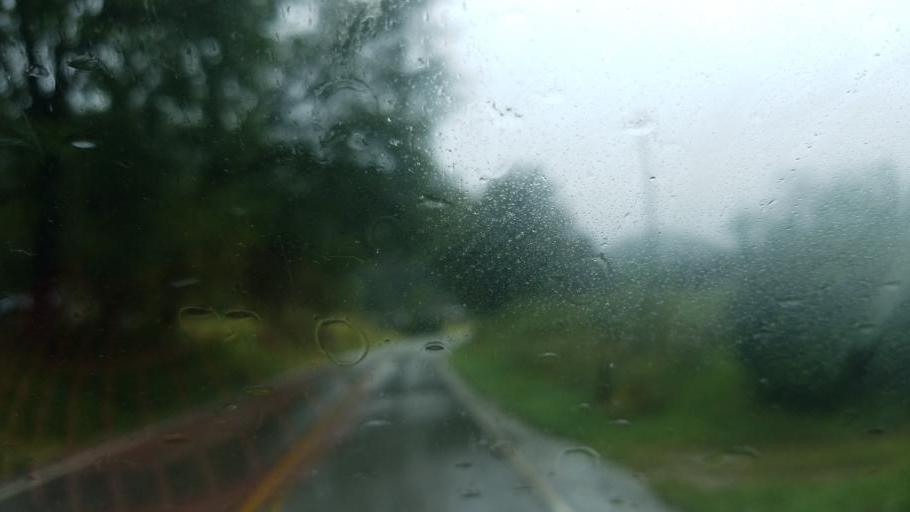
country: US
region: Kentucky
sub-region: Greenup County
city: South Shore
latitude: 38.6884
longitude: -82.9324
